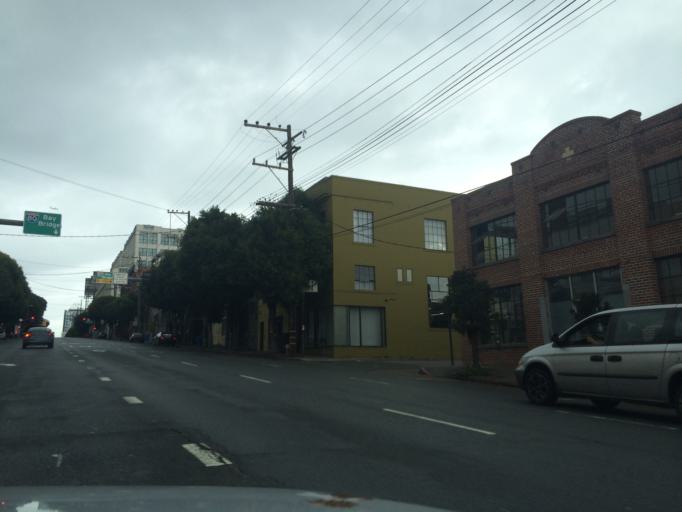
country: US
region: California
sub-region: San Francisco County
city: San Francisco
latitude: 37.7820
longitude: -122.3951
